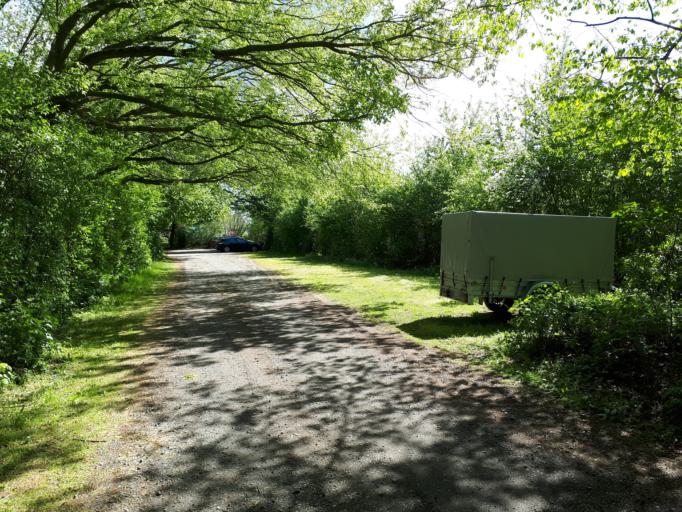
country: DE
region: Lower Saxony
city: Leiferde
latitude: 52.2221
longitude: 10.5382
